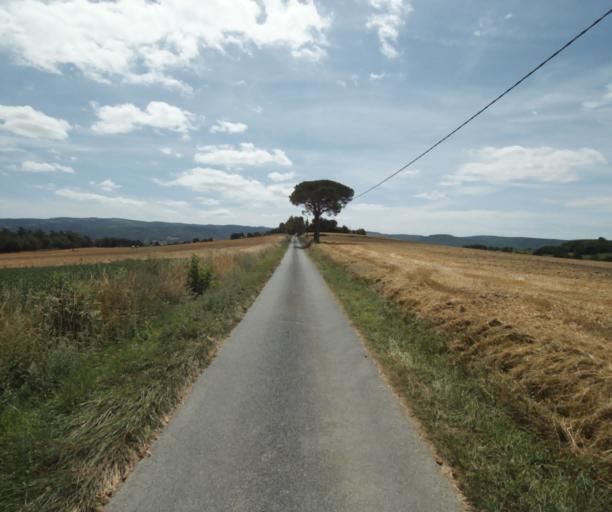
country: FR
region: Midi-Pyrenees
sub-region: Departement du Tarn
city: Soreze
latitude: 43.4945
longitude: 2.0663
